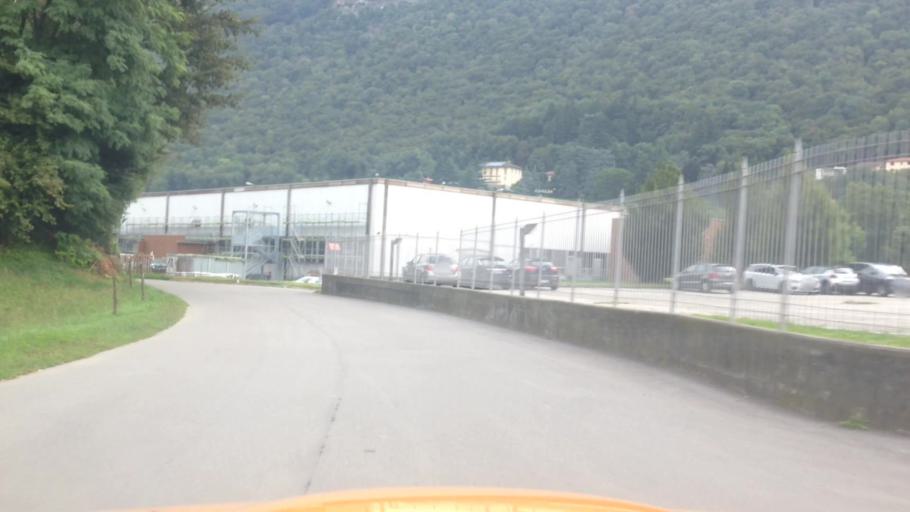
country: CH
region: Ticino
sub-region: Mendrisio District
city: Mendrisio
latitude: 45.8817
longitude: 8.9778
